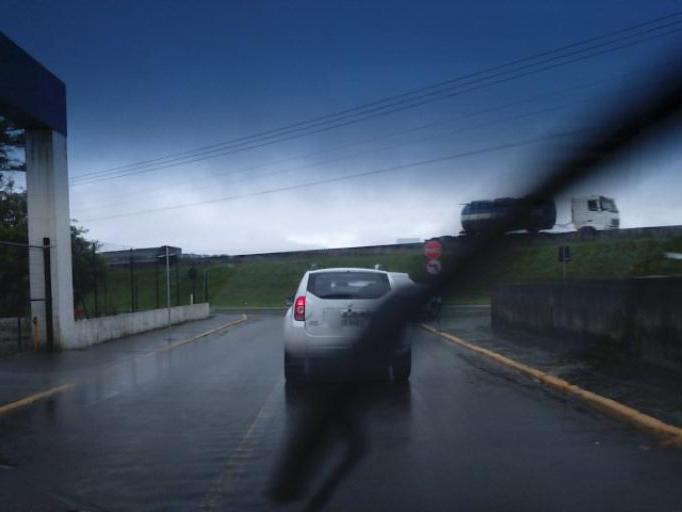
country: BR
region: Santa Catarina
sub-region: Itapema
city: Itapema
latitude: -27.1319
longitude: -48.6093
